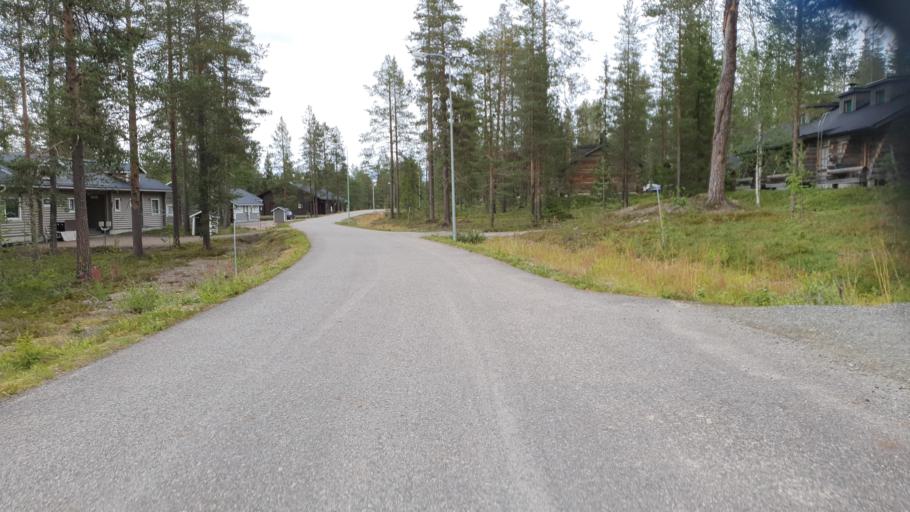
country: FI
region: Lapland
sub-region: Tunturi-Lappi
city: Kolari
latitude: 67.5933
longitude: 24.1476
